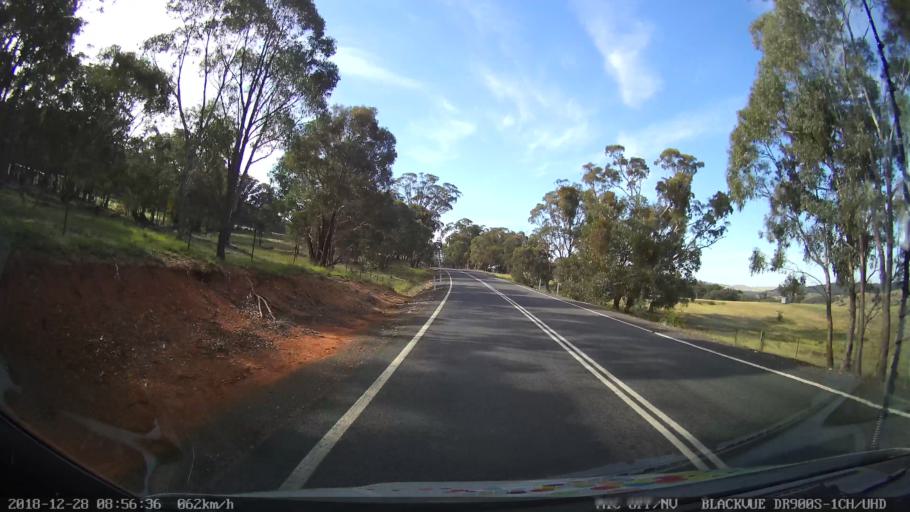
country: AU
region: New South Wales
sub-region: Upper Lachlan Shire
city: Crookwell
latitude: -34.1117
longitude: 149.3378
